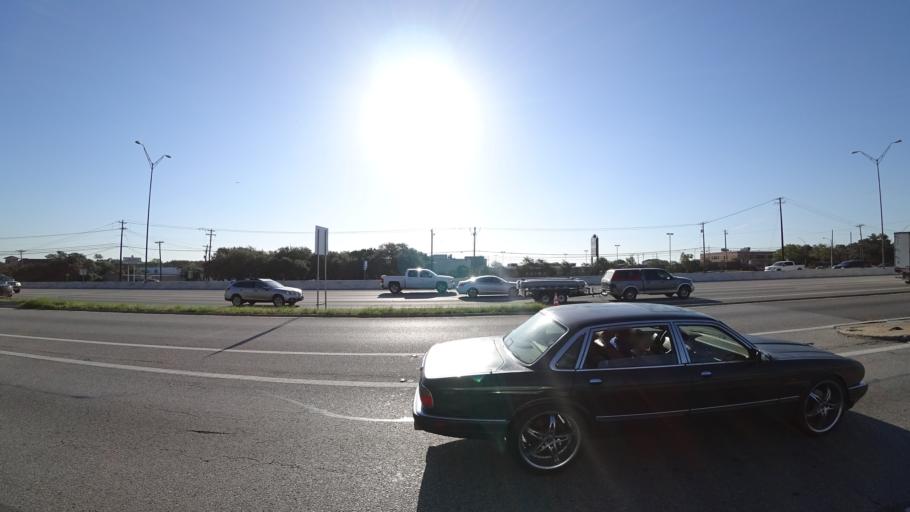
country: US
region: Texas
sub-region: Travis County
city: Austin
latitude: 30.3435
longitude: -97.6978
